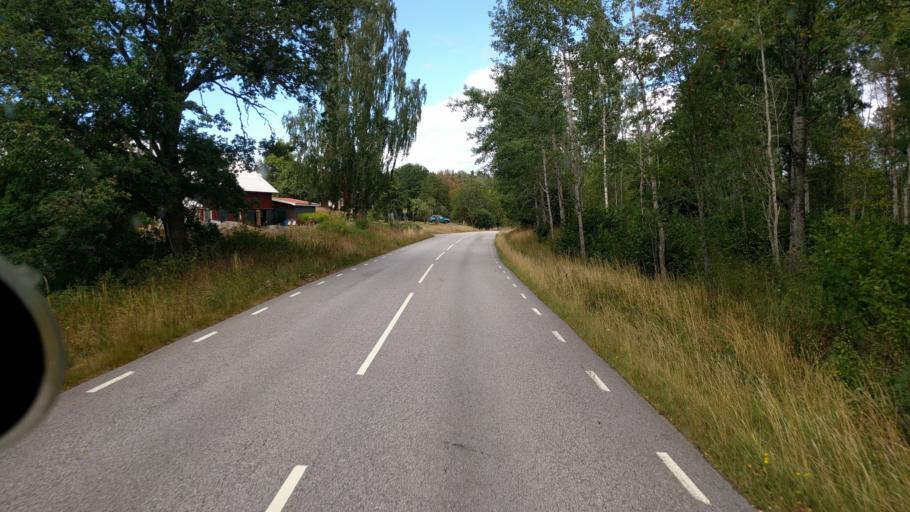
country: SE
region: Kalmar
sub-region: Vasterviks Kommun
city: Ankarsrum
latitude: 57.7570
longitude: 16.1245
